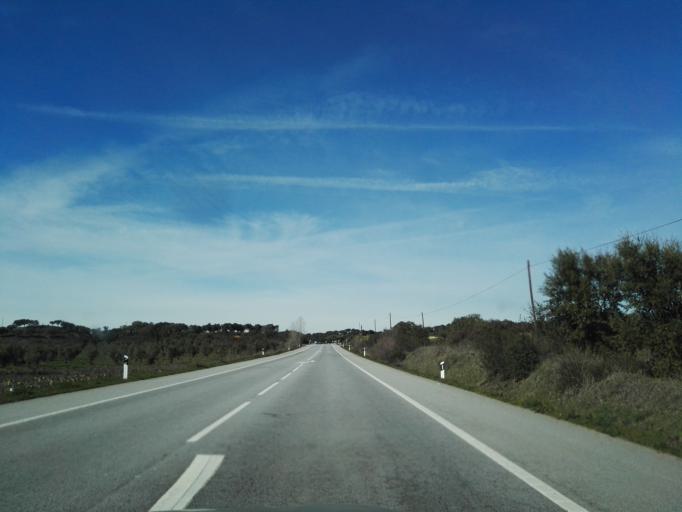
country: PT
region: Portalegre
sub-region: Portalegre
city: Urra
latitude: 39.1930
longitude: -7.3601
